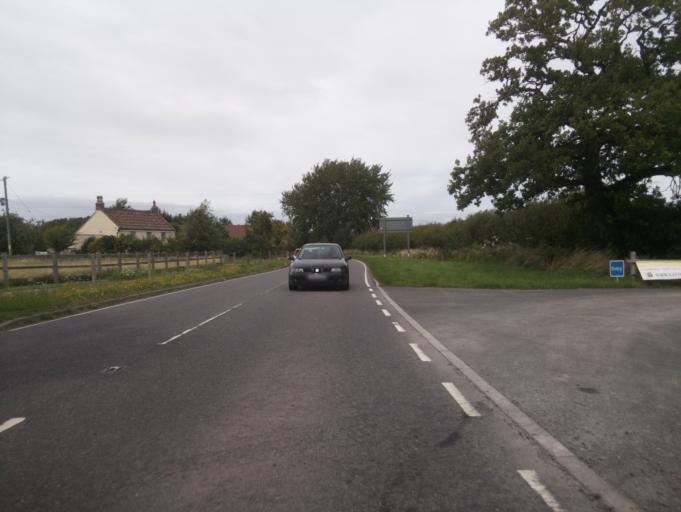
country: GB
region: England
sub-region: North Somerset
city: Kenn
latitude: 51.4027
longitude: -2.8422
